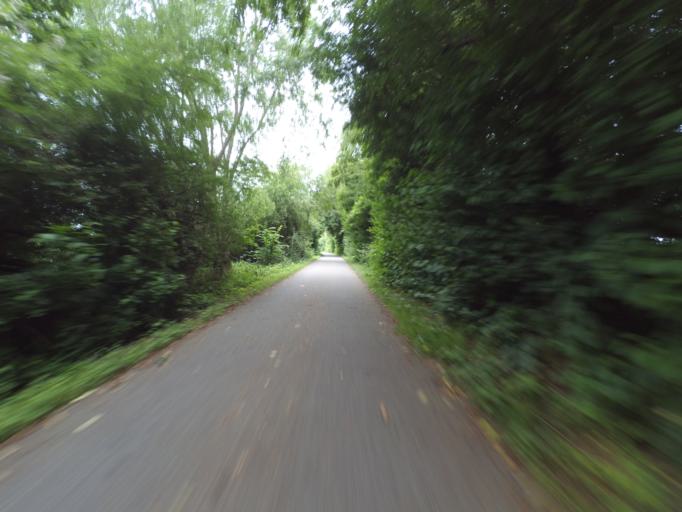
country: DE
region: North Rhine-Westphalia
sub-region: Regierungsbezirk Koln
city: Wurselen
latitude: 50.7702
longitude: 6.1485
